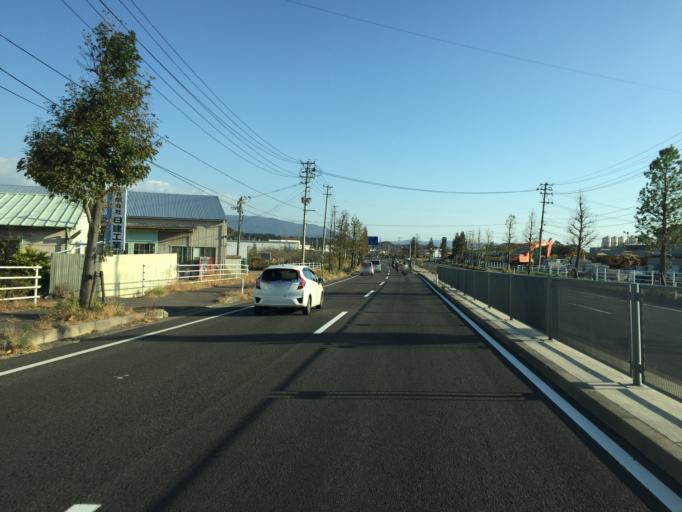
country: JP
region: Fukushima
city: Hobaramachi
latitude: 37.8329
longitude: 140.5169
